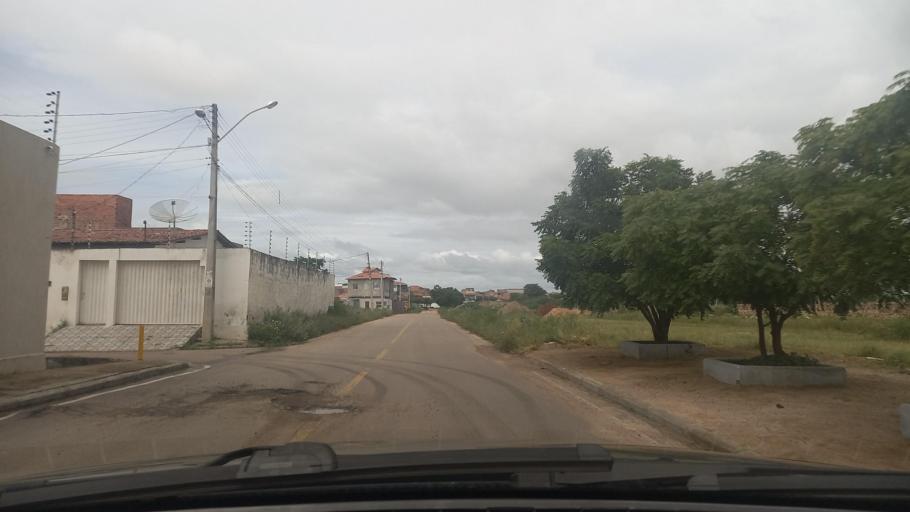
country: BR
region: Bahia
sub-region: Paulo Afonso
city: Paulo Afonso
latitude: -9.4030
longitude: -38.2420
